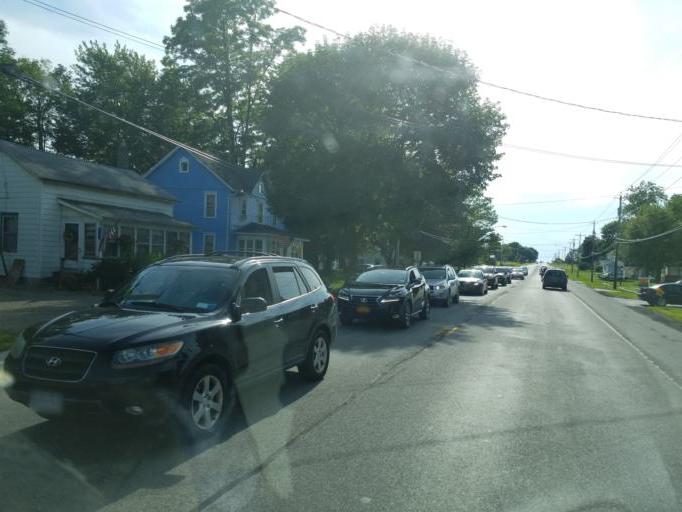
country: US
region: New York
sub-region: Genesee County
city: Le Roy
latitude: 42.9821
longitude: -78.0770
